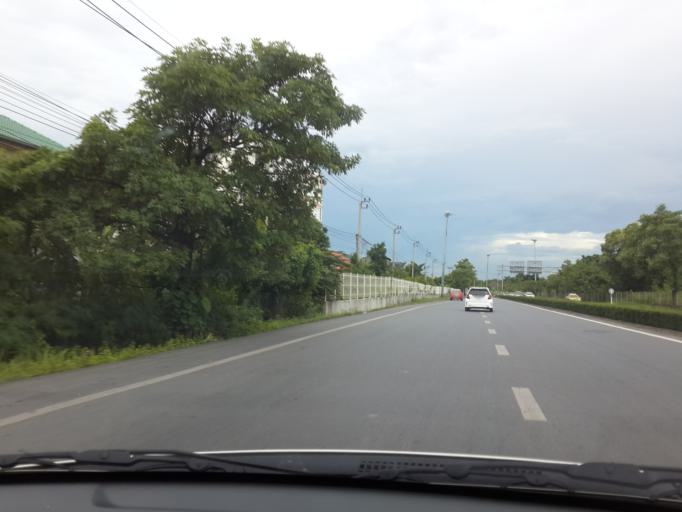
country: TH
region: Bangkok
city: Saphan Sung
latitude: 13.7834
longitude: 100.6876
